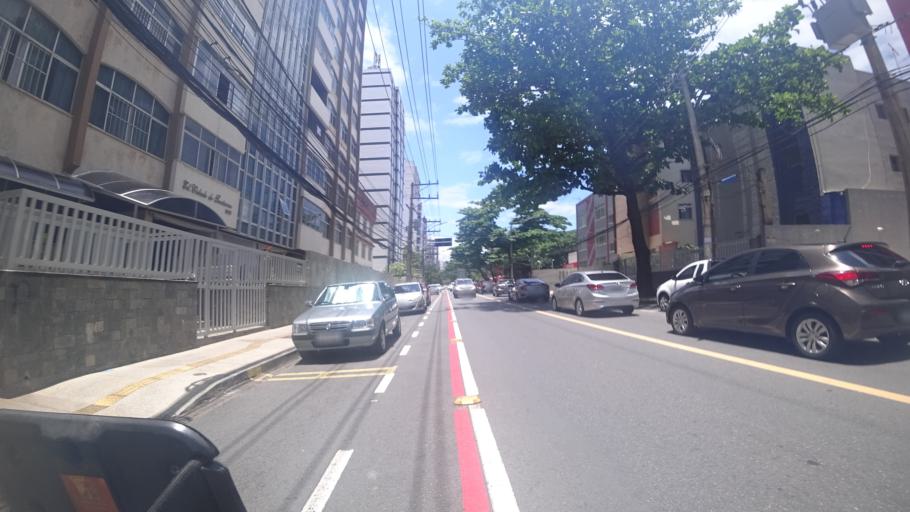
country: BR
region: Bahia
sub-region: Salvador
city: Salvador
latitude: -13.0053
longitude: -38.4614
